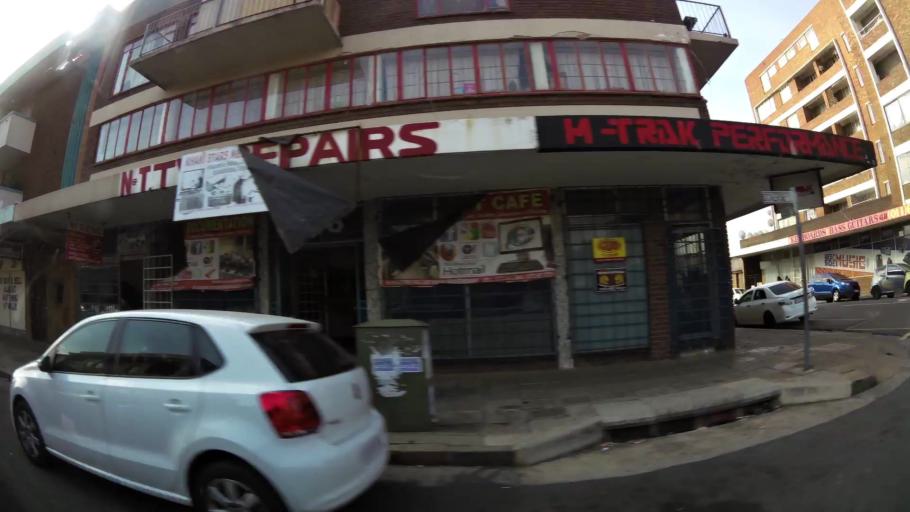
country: ZA
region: Gauteng
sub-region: West Rand District Municipality
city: Krugersdorp
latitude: -26.1031
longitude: 27.7741
